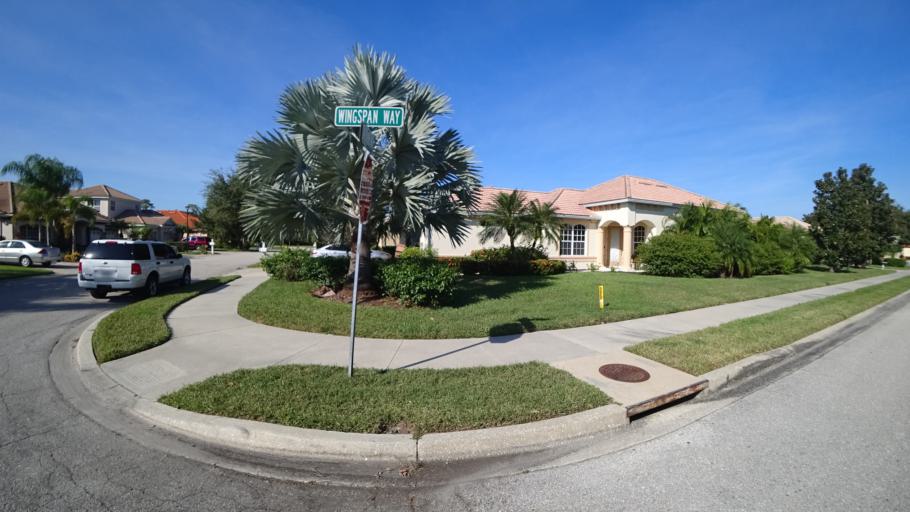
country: US
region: Florida
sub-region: Sarasota County
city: Desoto Lakes
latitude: 27.4262
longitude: -82.4624
